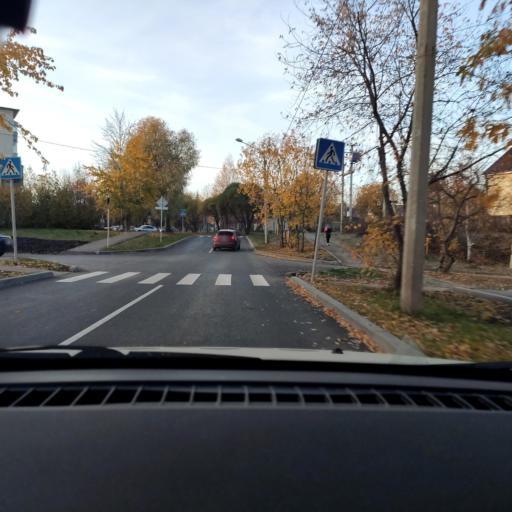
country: RU
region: Perm
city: Novyye Lyady
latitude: 58.0509
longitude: 56.5777
